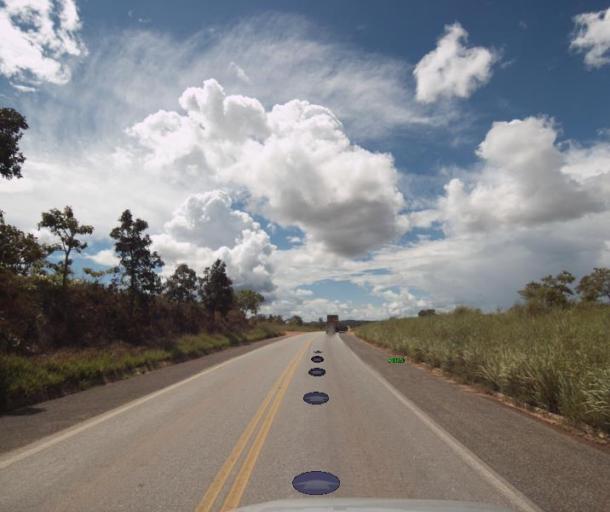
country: BR
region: Goias
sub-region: Uruacu
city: Uruacu
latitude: -14.0711
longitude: -49.0964
